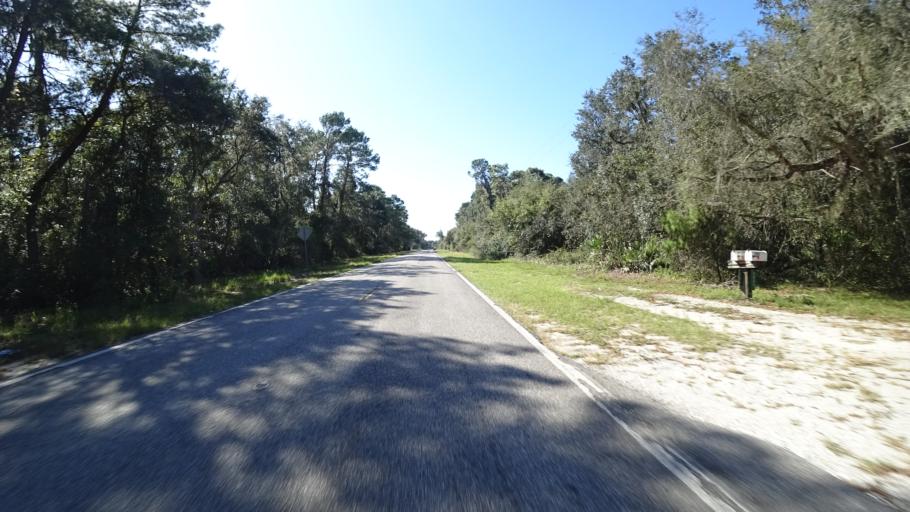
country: US
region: Florida
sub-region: Hillsborough County
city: Wimauma
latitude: 27.6555
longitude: -82.2942
